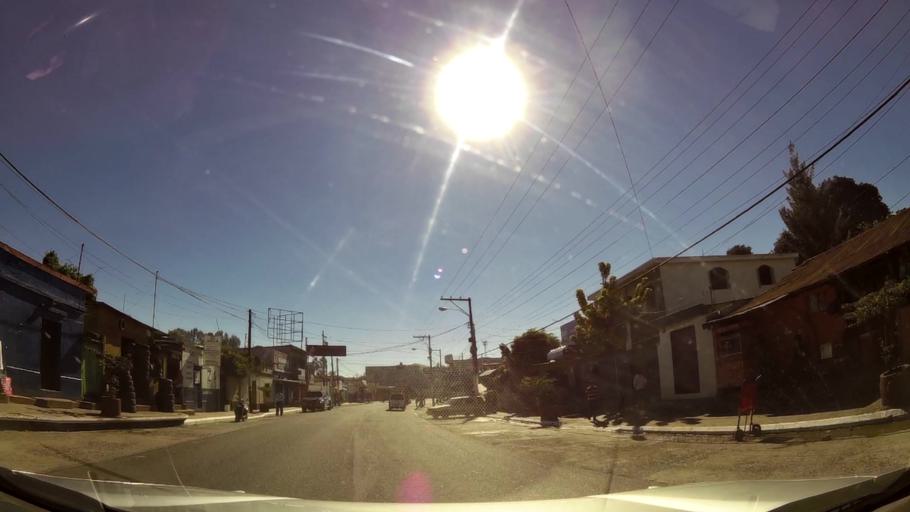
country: GT
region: Guatemala
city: Fraijanes
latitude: 14.4680
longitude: -90.4436
